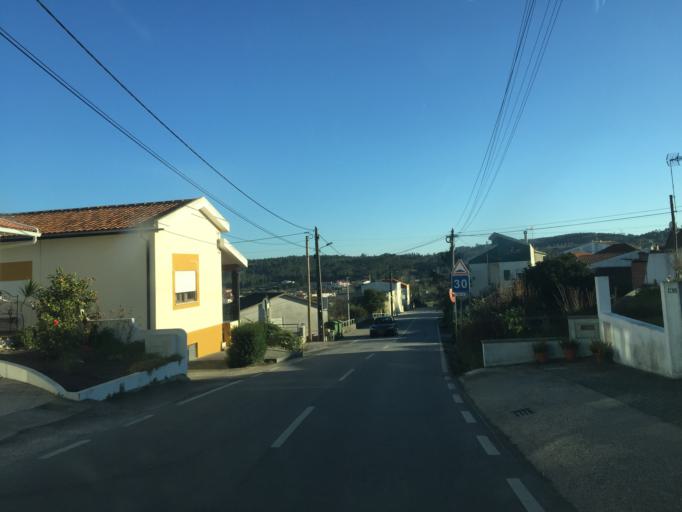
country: PT
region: Coimbra
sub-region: Figueira da Foz
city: Tavarede
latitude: 40.1658
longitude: -8.8197
